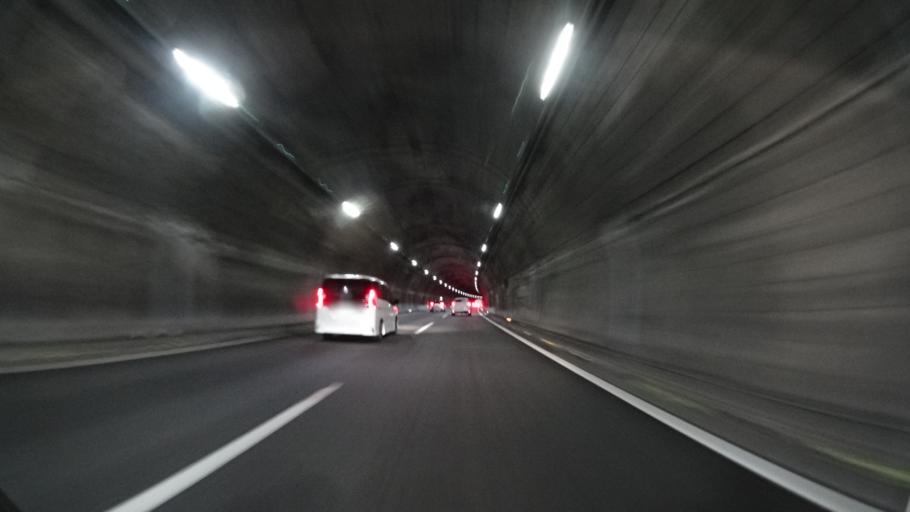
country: JP
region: Hyogo
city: Kariya
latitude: 34.7906
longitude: 134.4070
